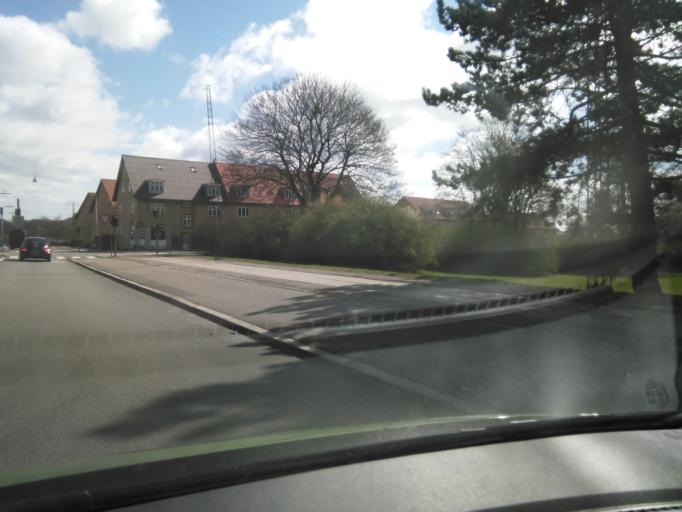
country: DK
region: Central Jutland
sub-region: Arhus Kommune
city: Arhus
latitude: 56.1756
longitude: 10.2095
